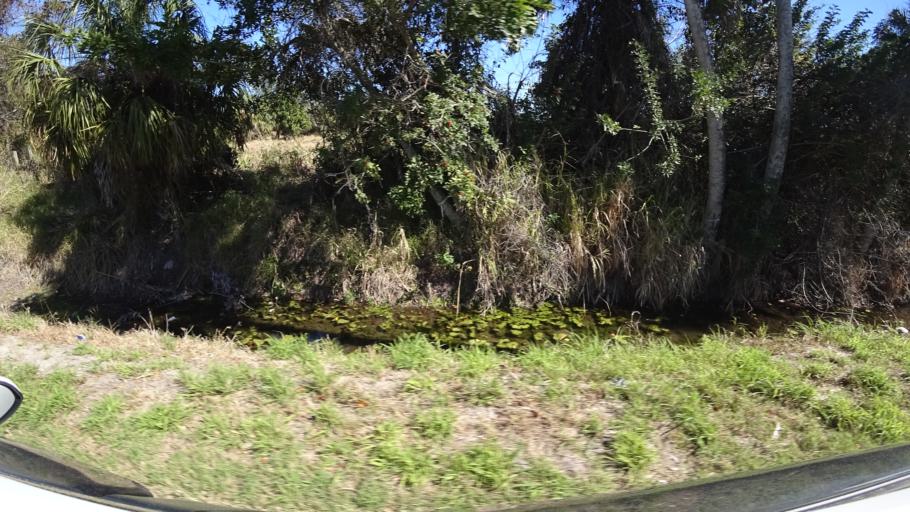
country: US
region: Florida
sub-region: Manatee County
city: Memphis
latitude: 27.5497
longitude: -82.5483
